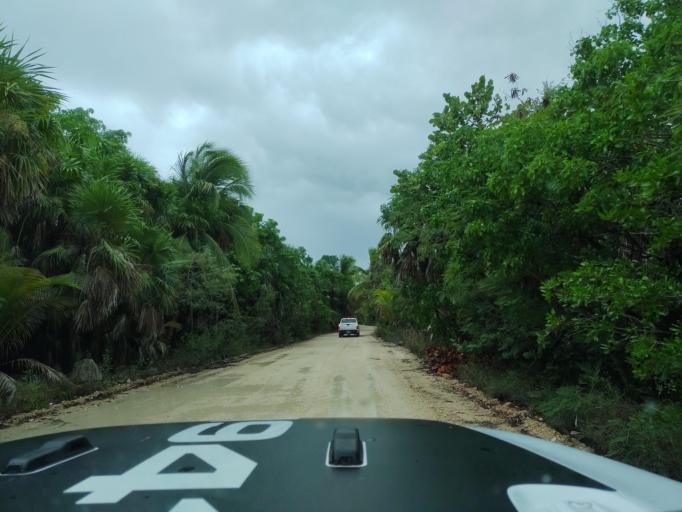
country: MX
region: Quintana Roo
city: Tulum
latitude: 20.0599
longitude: -87.4808
